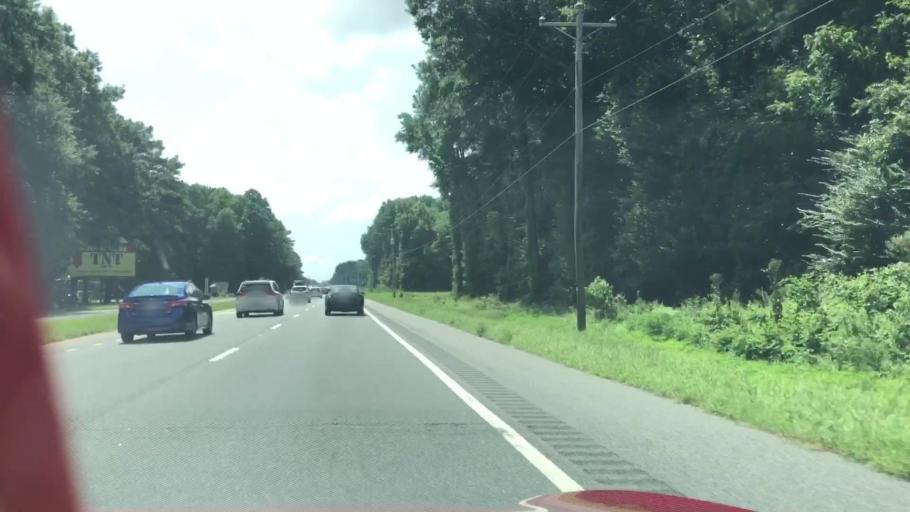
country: US
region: Virginia
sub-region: Northampton County
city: Cape Charles
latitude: 37.2602
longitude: -75.9739
